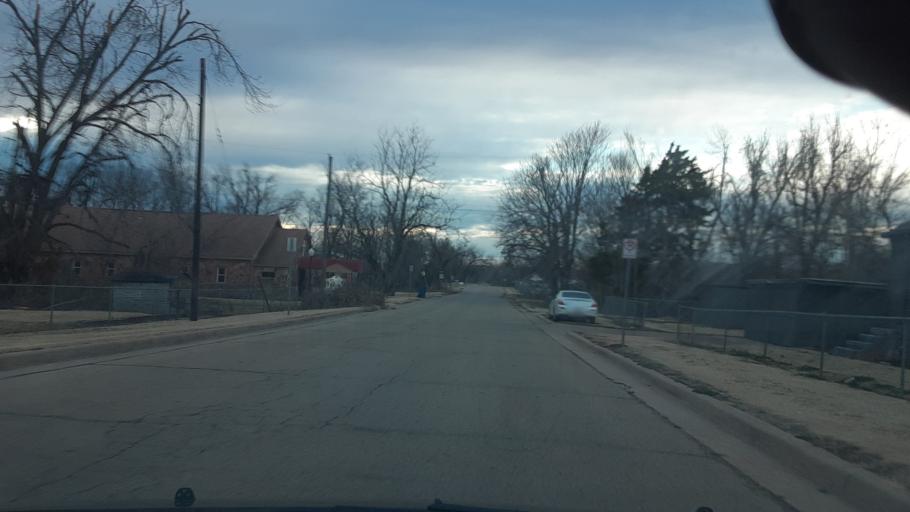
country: US
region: Oklahoma
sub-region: Logan County
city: Guthrie
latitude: 35.8729
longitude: -97.4229
